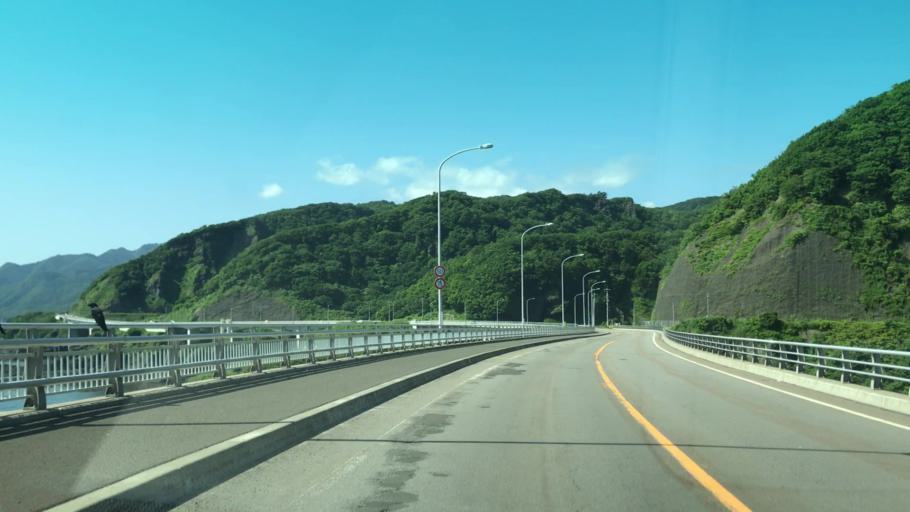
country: JP
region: Hokkaido
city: Iwanai
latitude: 43.1243
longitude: 140.4429
